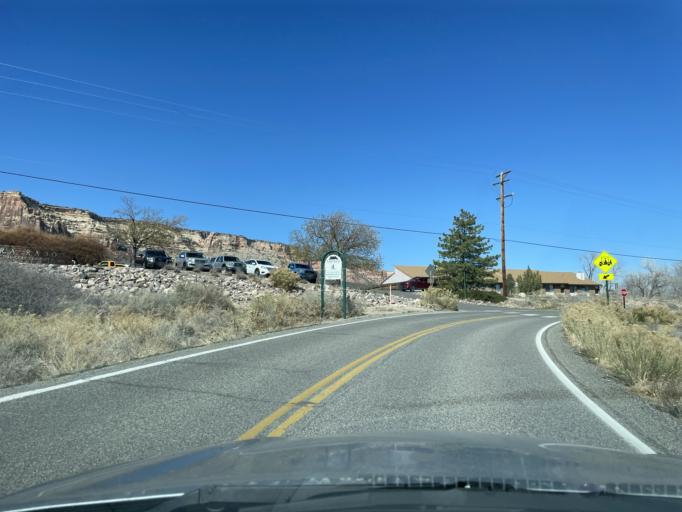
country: US
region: Colorado
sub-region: Mesa County
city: Redlands
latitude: 39.0780
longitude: -108.6684
